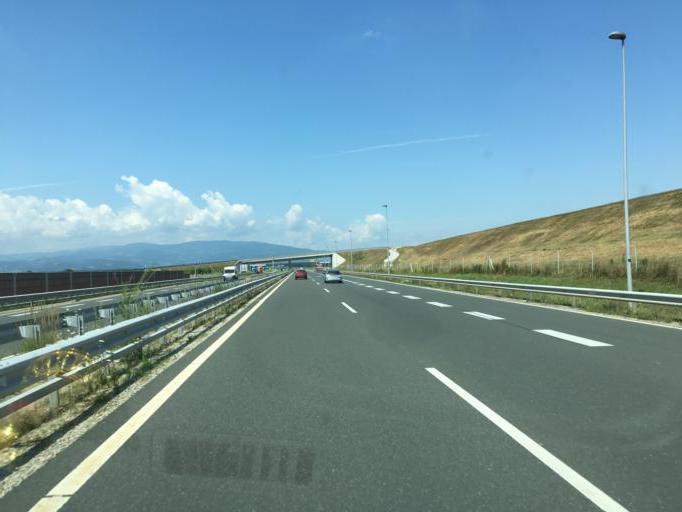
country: SI
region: Starse
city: Starse
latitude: 46.4502
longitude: 15.7648
